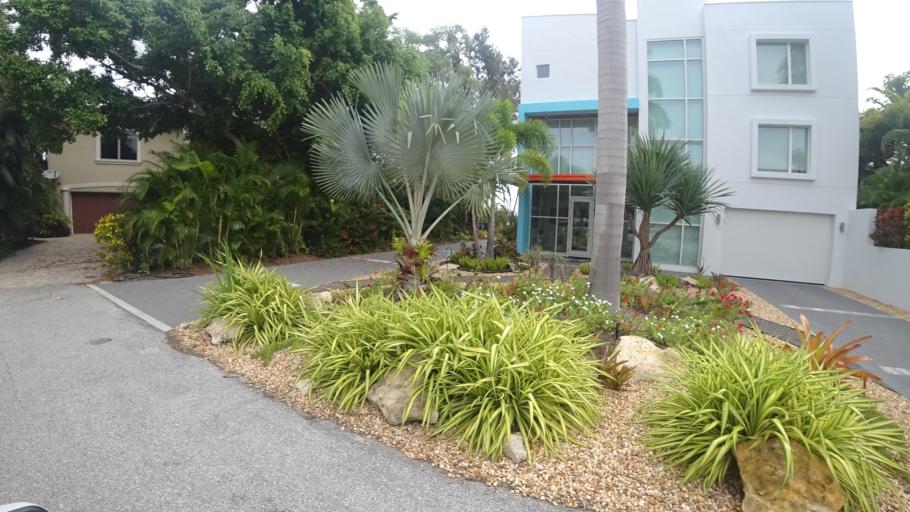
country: US
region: Florida
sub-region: Manatee County
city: Longboat Key
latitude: 27.4307
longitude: -82.6706
